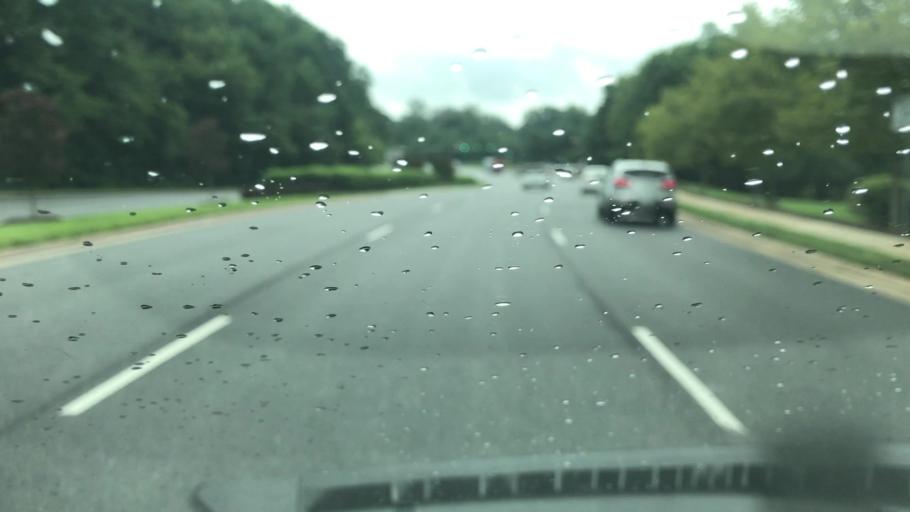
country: US
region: Virginia
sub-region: Fairfax County
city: Greenbriar
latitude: 38.8619
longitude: -77.3800
